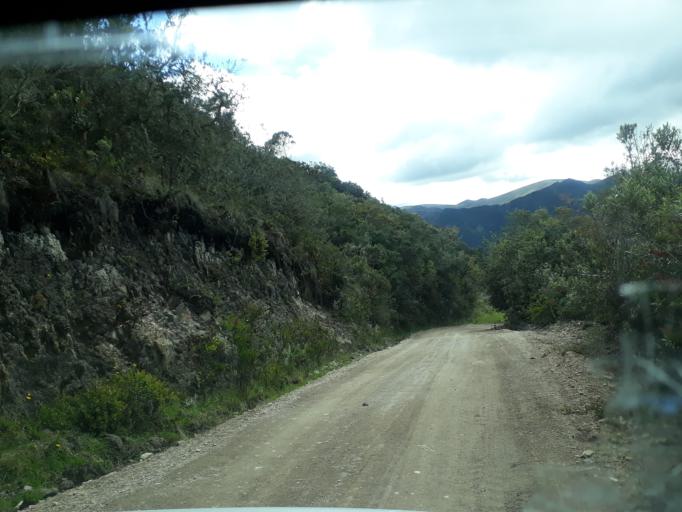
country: CO
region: Cundinamarca
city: La Mesa
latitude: 5.2571
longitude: -73.8988
